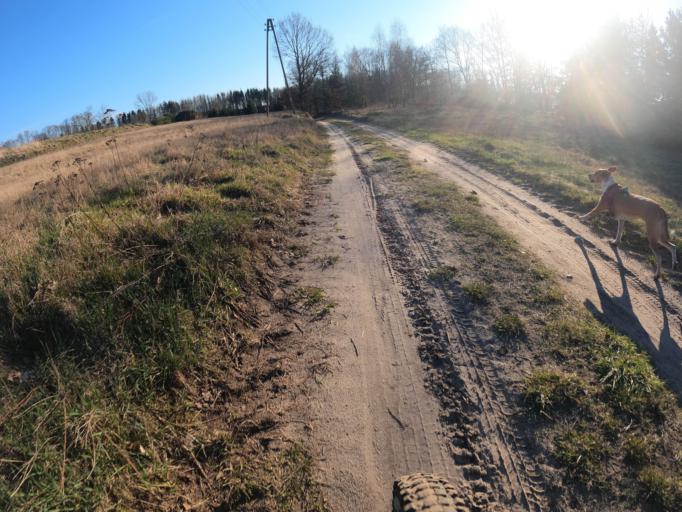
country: PL
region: West Pomeranian Voivodeship
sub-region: Powiat gryficki
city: Brojce
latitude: 53.9563
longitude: 15.4227
